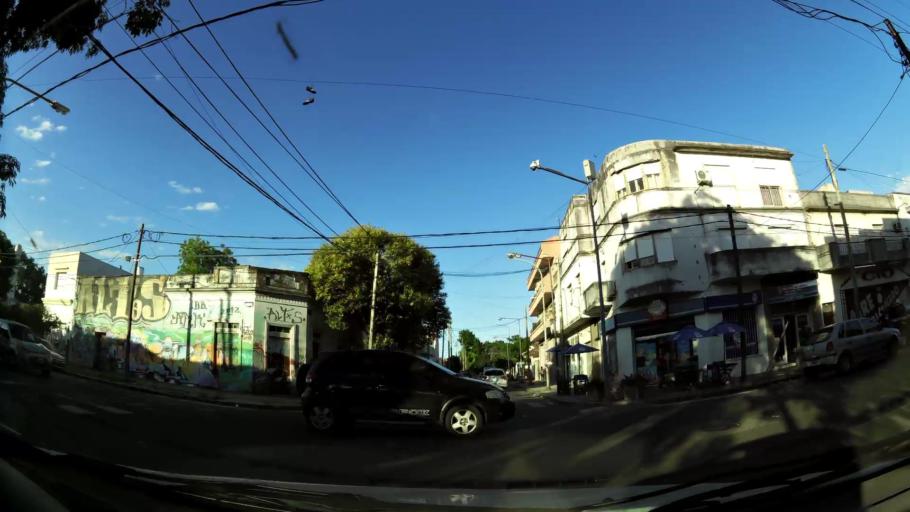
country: AR
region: Buenos Aires
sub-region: Partido de General San Martin
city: General San Martin
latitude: -34.5703
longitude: -58.5473
